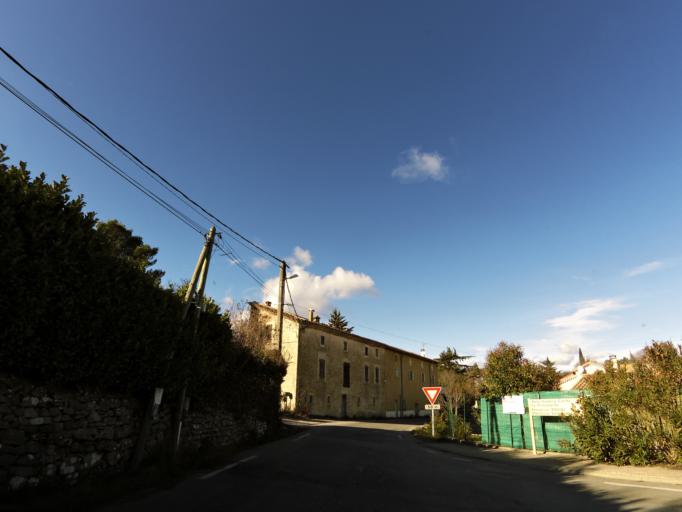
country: FR
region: Languedoc-Roussillon
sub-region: Departement du Gard
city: Sauve
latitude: 43.9881
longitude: 3.9514
